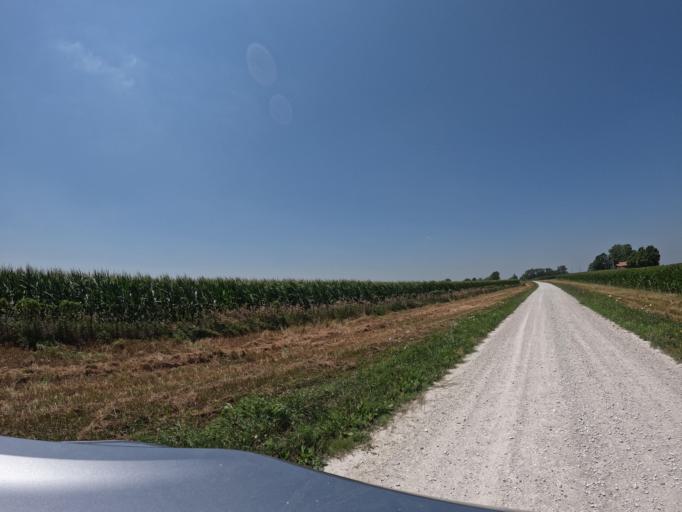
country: US
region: Iowa
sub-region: Keokuk County
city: Sigourney
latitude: 41.2747
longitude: -92.1592
